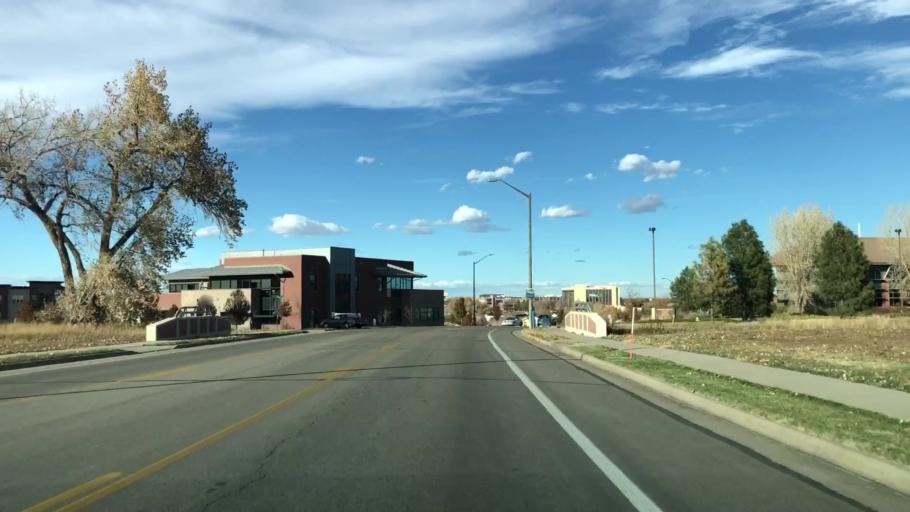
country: US
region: Colorado
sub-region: Larimer County
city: Fort Collins
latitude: 40.5581
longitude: -105.0873
